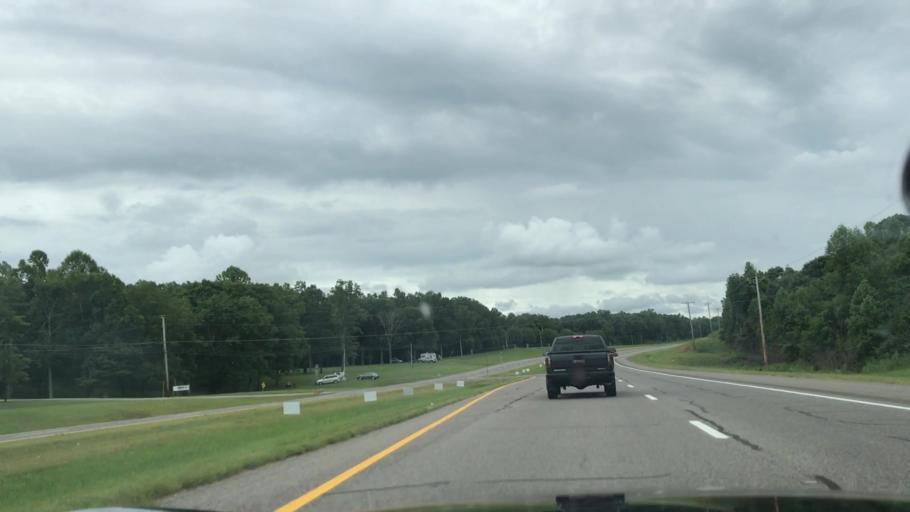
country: US
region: Tennessee
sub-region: Fentress County
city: Jamestown
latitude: 36.3725
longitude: -84.9442
